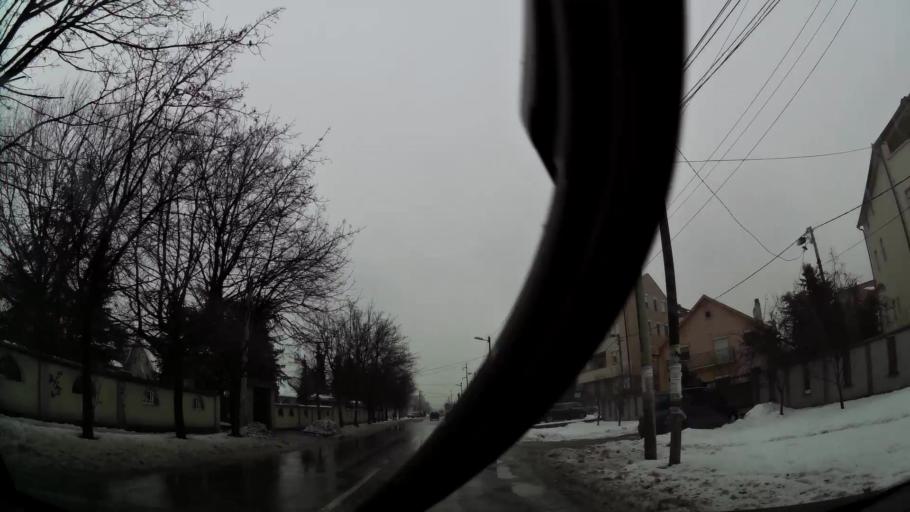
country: RS
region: Central Serbia
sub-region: Belgrade
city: Zemun
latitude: 44.8490
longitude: 20.3689
